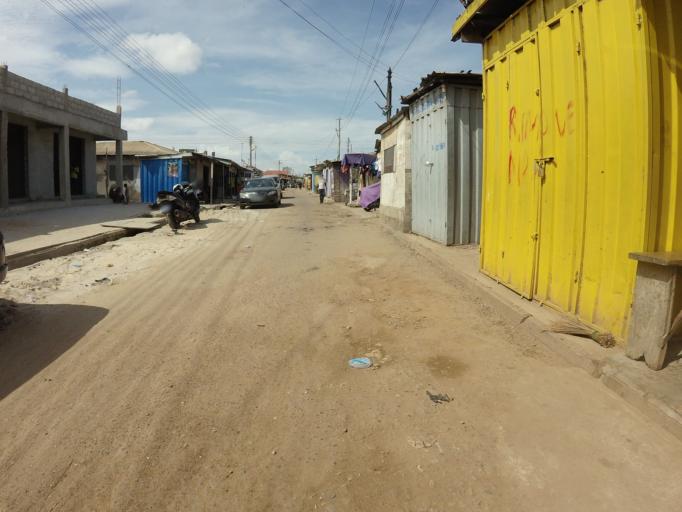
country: GH
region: Greater Accra
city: Accra
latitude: 5.5918
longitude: -0.1914
